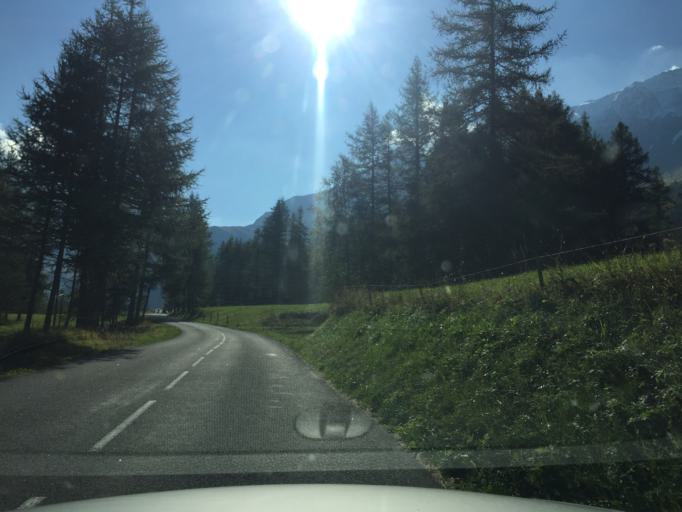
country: FR
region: Rhone-Alpes
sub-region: Departement de la Savoie
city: Belle-Plagne
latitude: 45.5267
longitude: 6.7869
